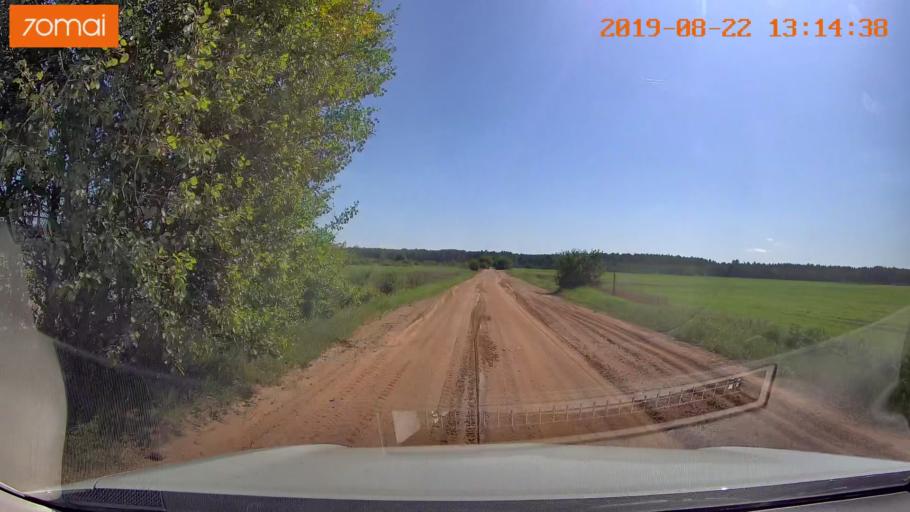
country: BY
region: Minsk
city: Prawdzinski
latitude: 53.2662
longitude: 27.8893
